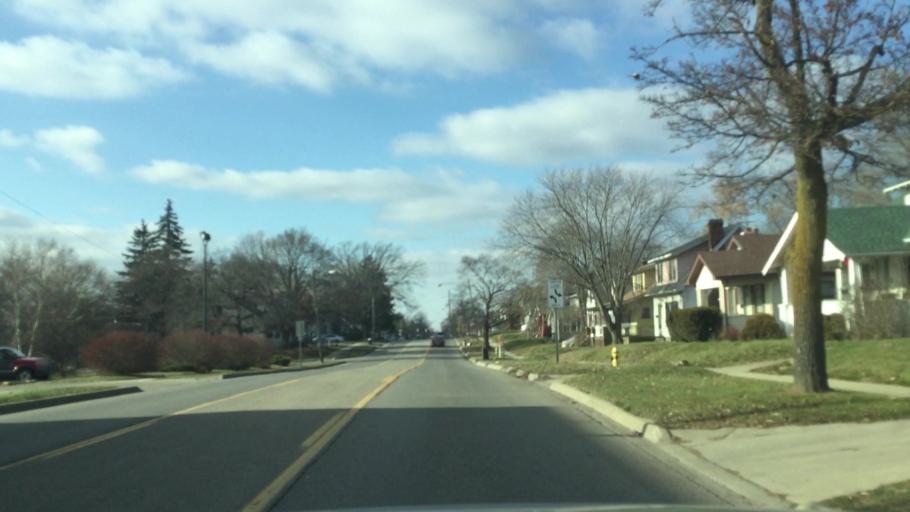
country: US
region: Michigan
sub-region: Genesee County
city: Flint
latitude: 43.0206
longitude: -83.7178
